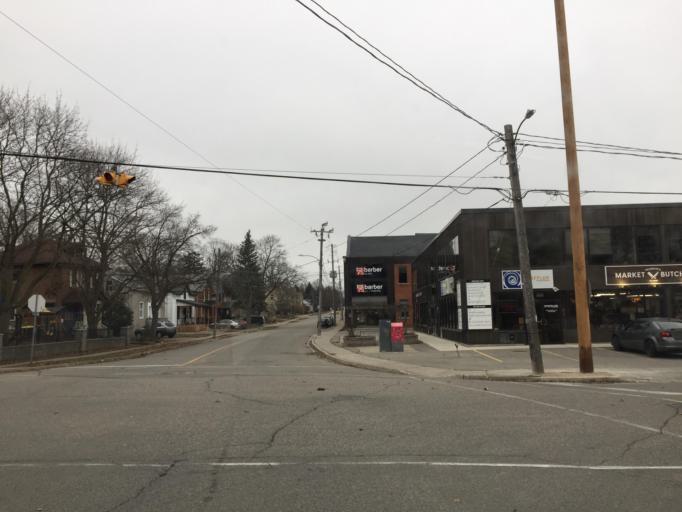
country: CA
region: Ontario
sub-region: Wellington County
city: Guelph
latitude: 43.5447
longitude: -80.2601
